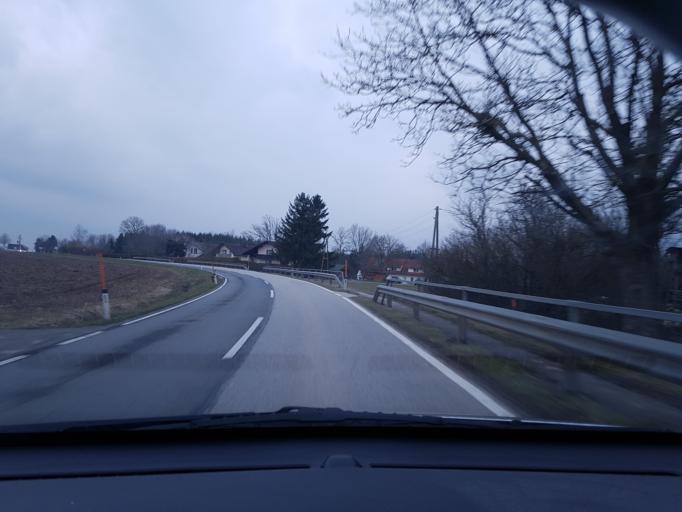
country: AT
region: Upper Austria
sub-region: Politischer Bezirk Steyr-Land
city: Sierning
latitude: 48.1235
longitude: 14.3451
